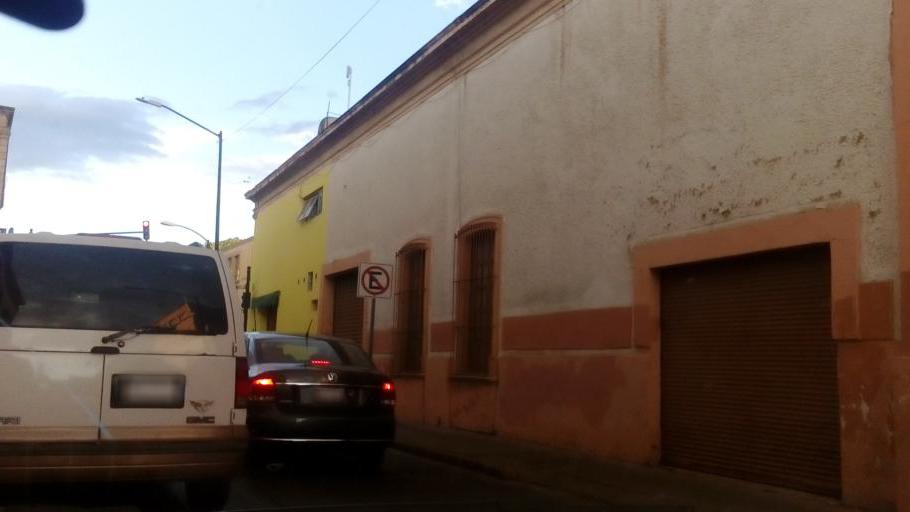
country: MX
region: Guanajuato
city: Leon
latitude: 21.1225
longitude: -101.6792
